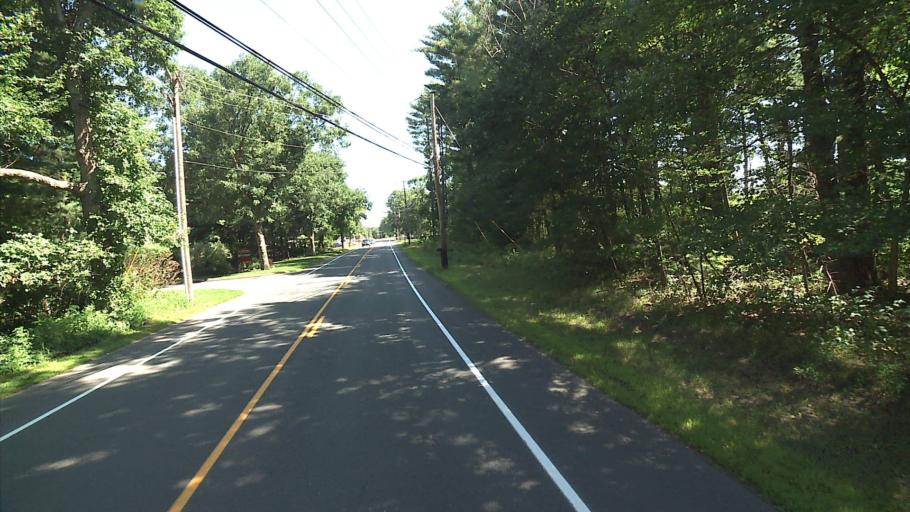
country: US
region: Connecticut
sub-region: Hartford County
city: North Granby
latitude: 41.9916
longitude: -72.7993
